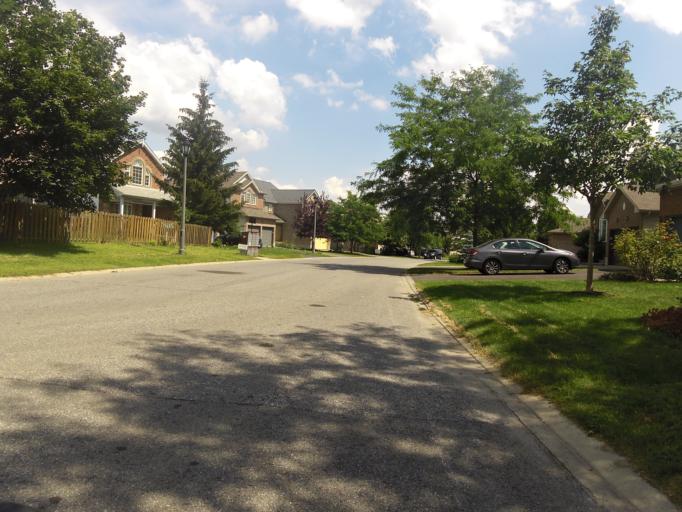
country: CA
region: Ontario
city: Bells Corners
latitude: 45.3175
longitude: -75.9280
